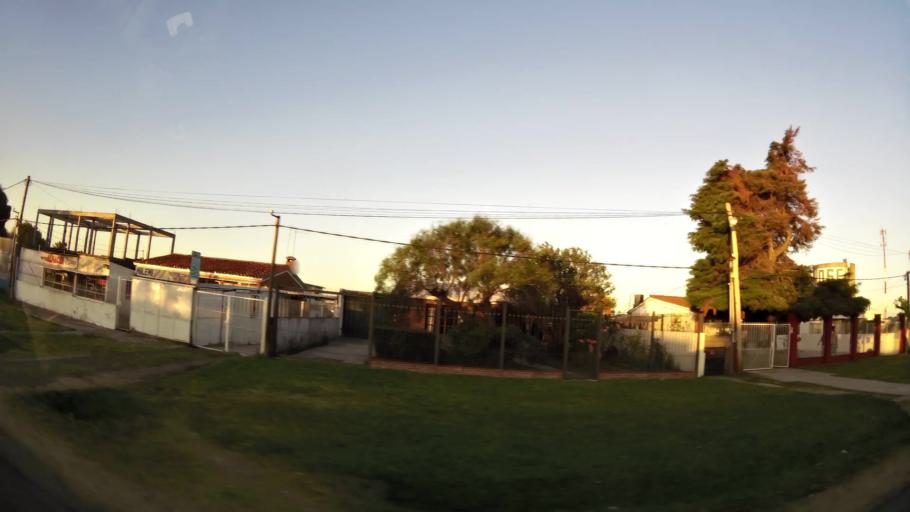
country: UY
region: Montevideo
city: Montevideo
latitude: -34.8272
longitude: -56.1576
